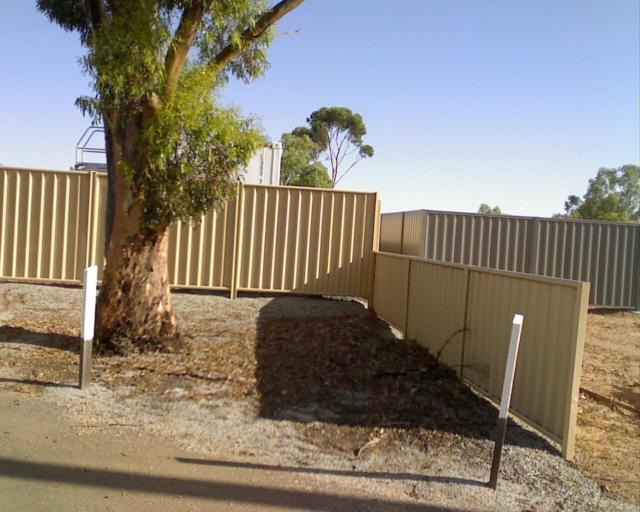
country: AU
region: Western Australia
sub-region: Merredin
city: Merredin
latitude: -31.1130
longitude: 117.7956
